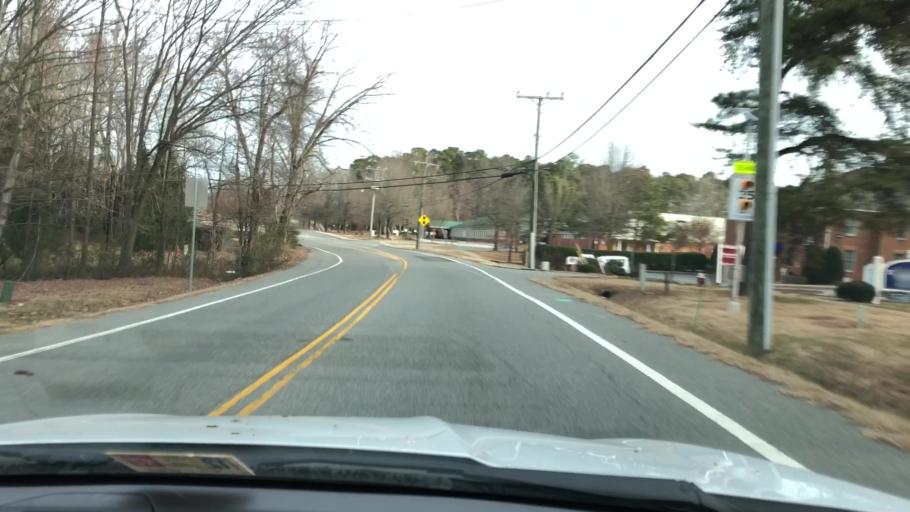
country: US
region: Virginia
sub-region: James City County
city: Williamsburg
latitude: 37.2718
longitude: -76.7390
